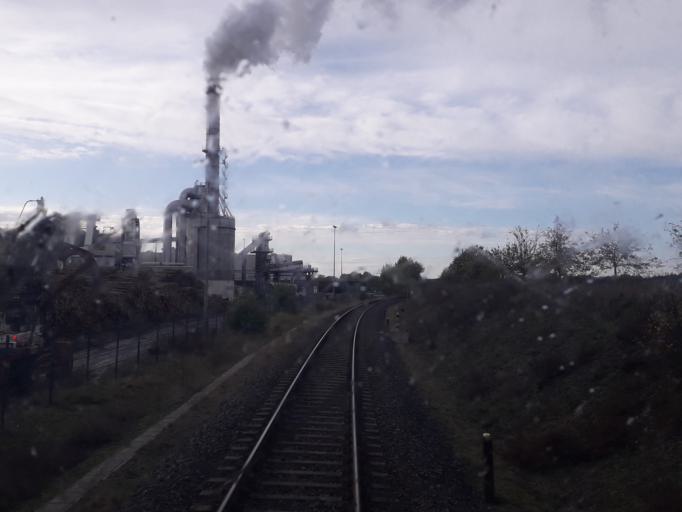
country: DE
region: Brandenburg
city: Heiligengrabe
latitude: 53.1517
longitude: 12.3804
